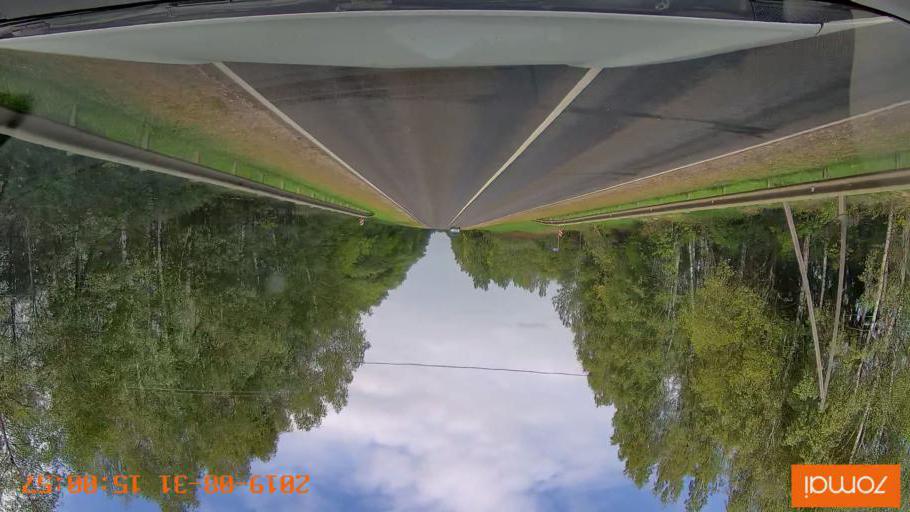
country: RU
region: Kaluga
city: Spas-Demensk
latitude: 54.3358
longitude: 34.0442
